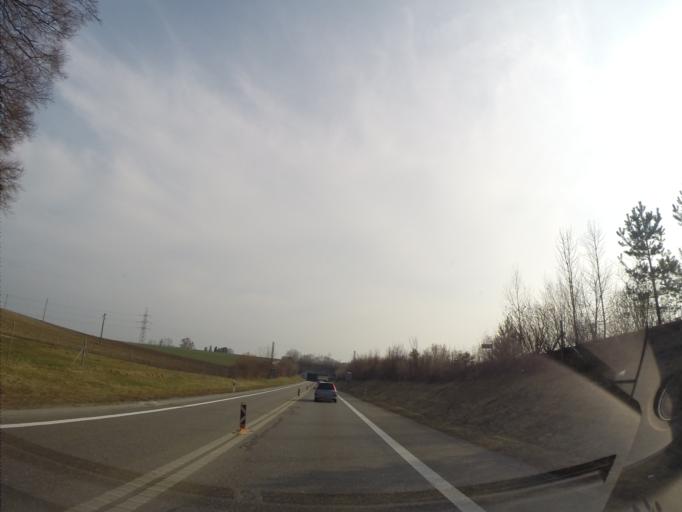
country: CH
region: Zurich
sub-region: Bezirk Andelfingen
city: Henggart
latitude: 47.5482
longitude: 8.6878
